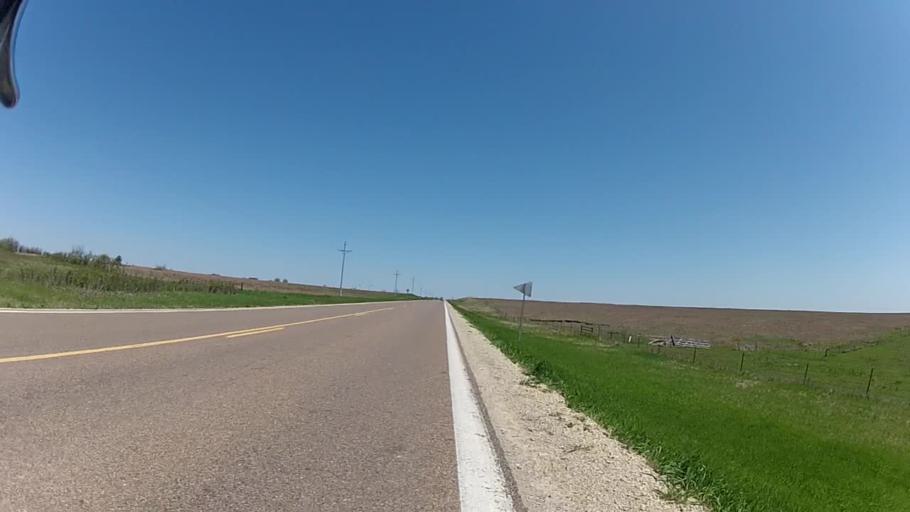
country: US
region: Kansas
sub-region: Wabaunsee County
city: Alma
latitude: 38.9347
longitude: -96.5202
